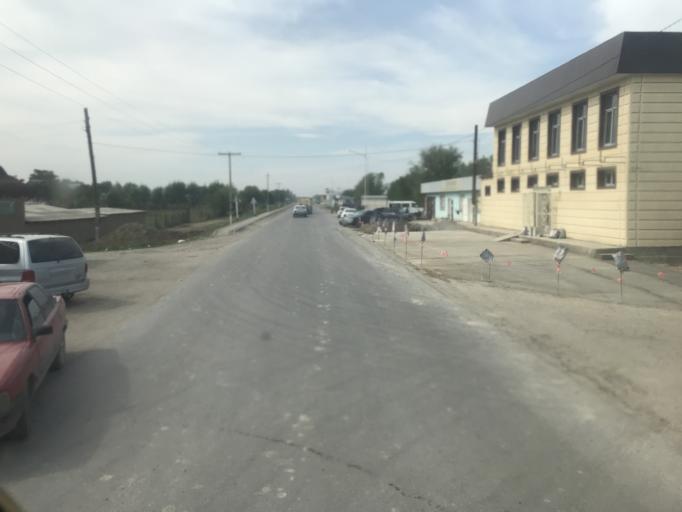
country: KZ
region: Ongtustik Qazaqstan
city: Asykata
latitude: 41.0052
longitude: 68.2148
